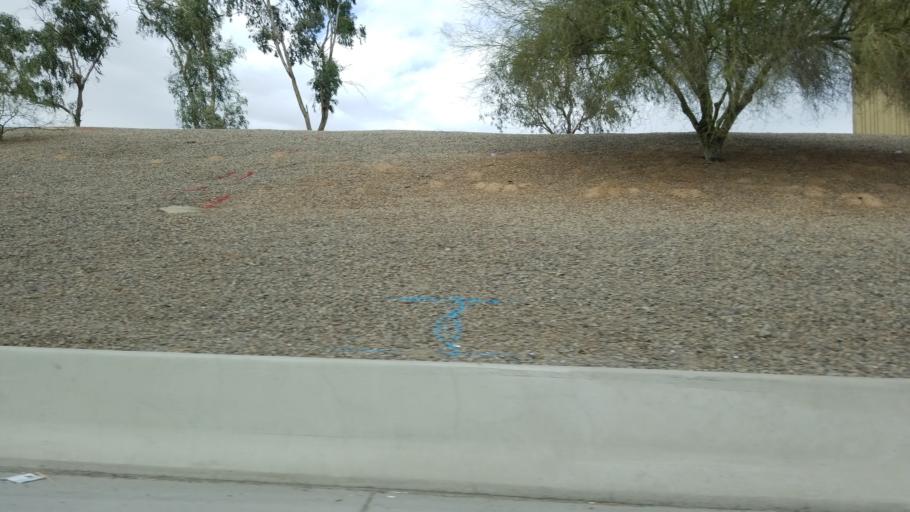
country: US
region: Arizona
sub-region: Maricopa County
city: Tolleson
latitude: 33.4630
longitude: -112.2138
